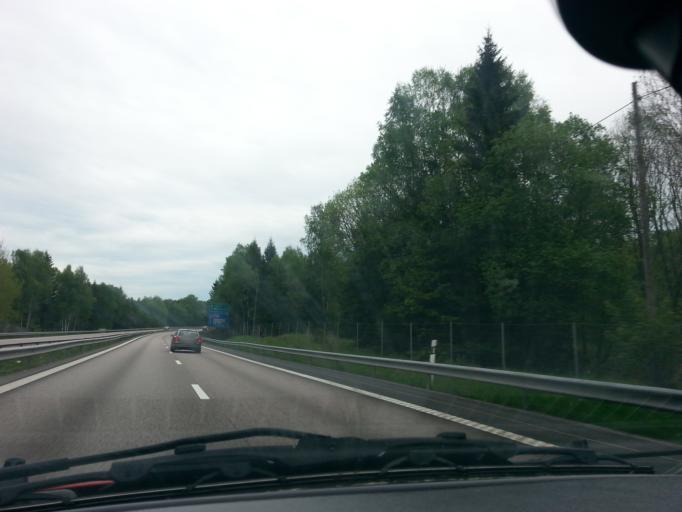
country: SE
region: Vaestra Goetaland
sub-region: Lerums Kommun
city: Lerum
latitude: 57.7452
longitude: 12.2234
